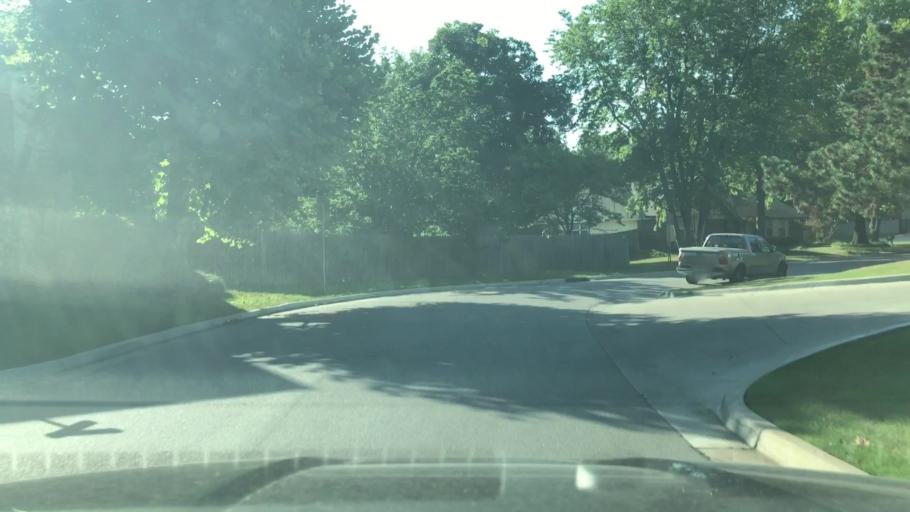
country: US
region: Oklahoma
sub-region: Tulsa County
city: Jenks
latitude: 36.0308
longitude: -95.9001
